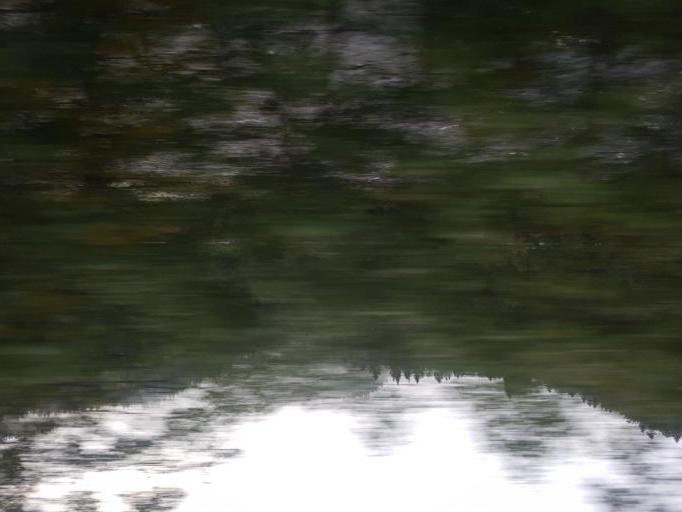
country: NO
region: Sor-Trondelag
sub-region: Midtre Gauldal
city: Storen
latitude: 63.0514
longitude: 10.2870
